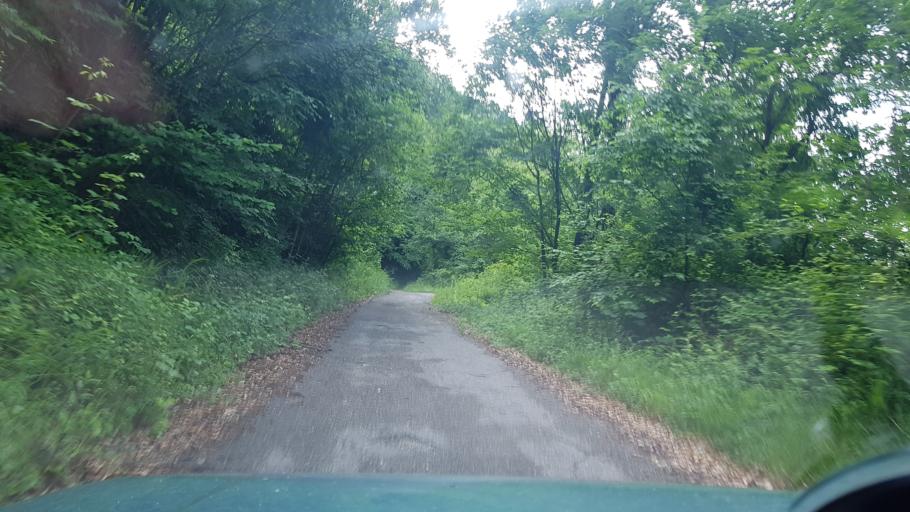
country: IT
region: Friuli Venezia Giulia
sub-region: Provincia di Udine
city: Torreano
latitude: 46.1635
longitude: 13.4416
